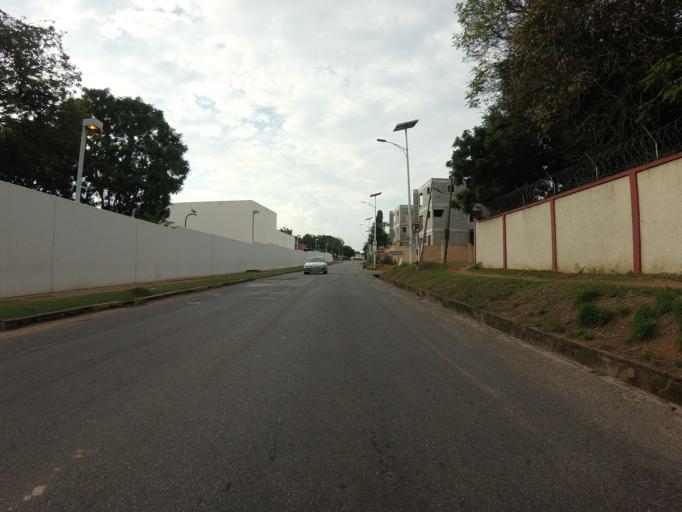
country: GH
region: Greater Accra
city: Accra
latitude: 5.5799
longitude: -0.1698
